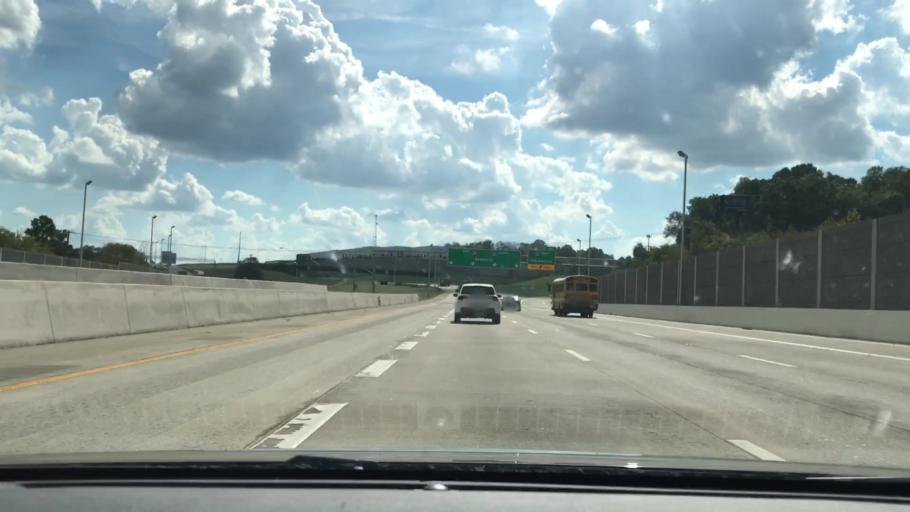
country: US
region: Tennessee
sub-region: Davidson County
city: Nashville
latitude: 36.2294
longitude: -86.7720
